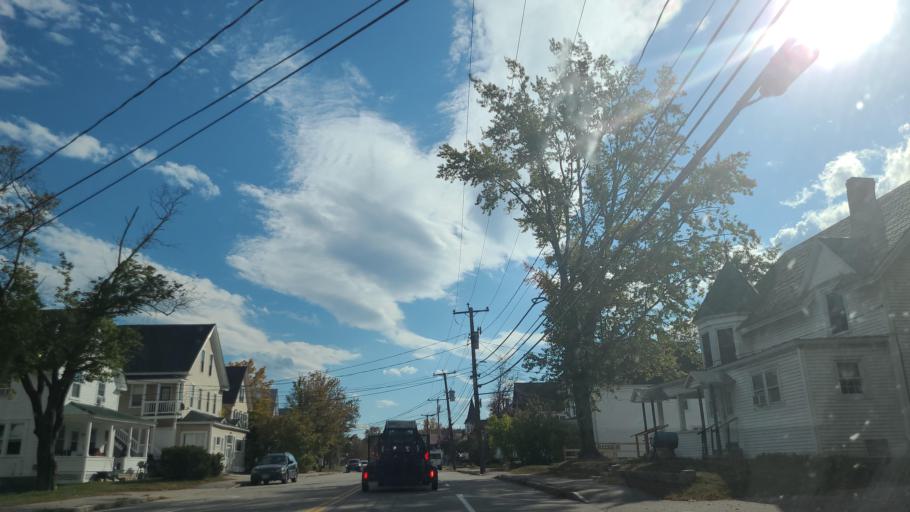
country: US
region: New Hampshire
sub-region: Carroll County
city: Conway
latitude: 43.9817
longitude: -71.1187
